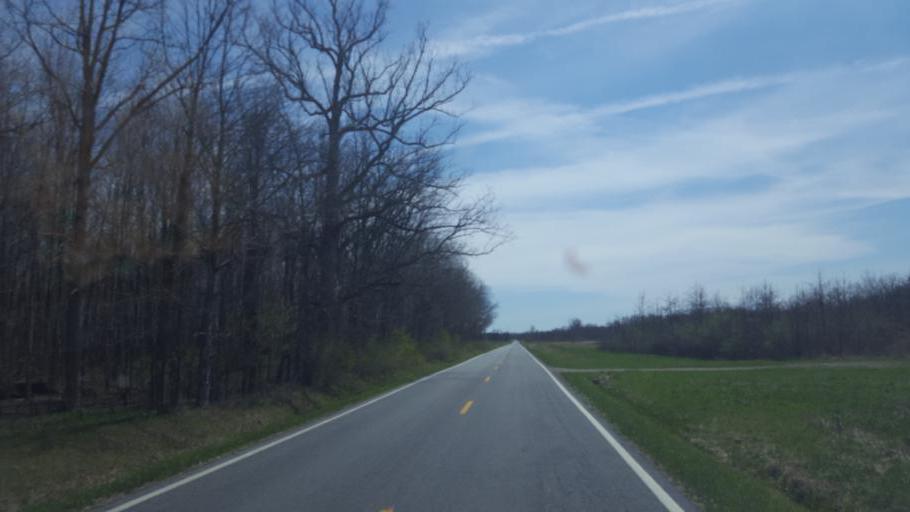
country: US
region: Ohio
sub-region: Delaware County
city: Ashley
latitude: 40.3943
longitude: -83.0383
